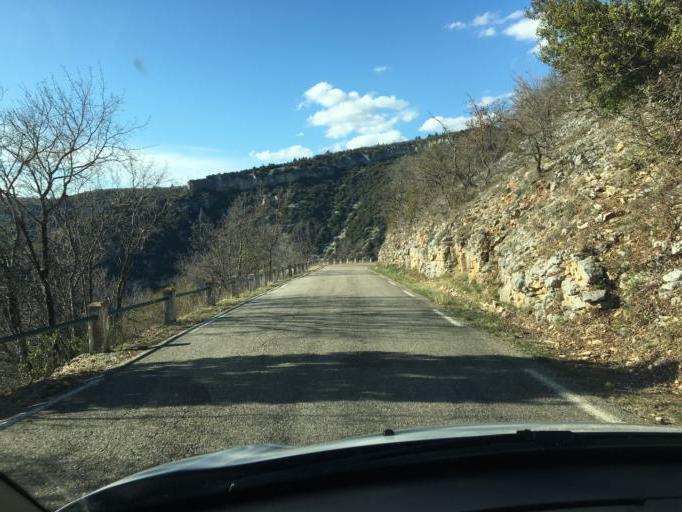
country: FR
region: Provence-Alpes-Cote d'Azur
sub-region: Departement du Vaucluse
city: Villes-sur-Auzon
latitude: 44.0622
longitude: 5.3203
